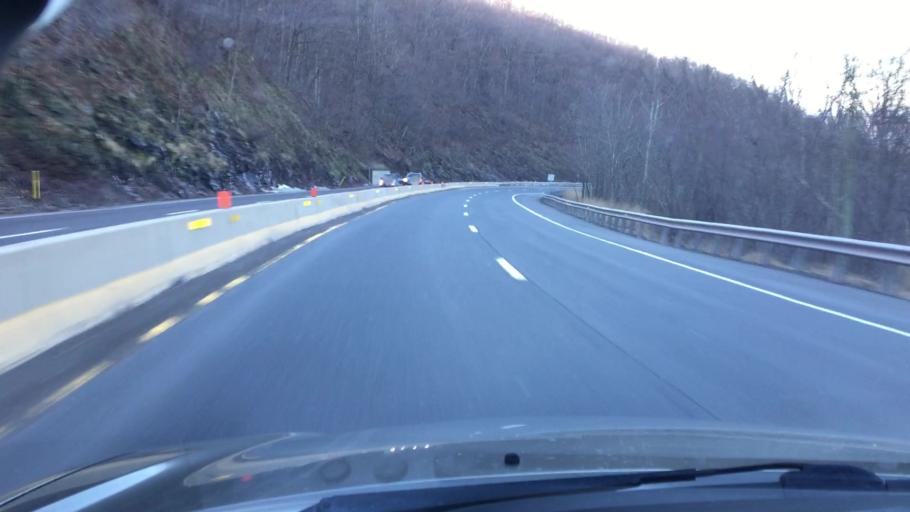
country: US
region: Pennsylvania
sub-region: Luzerne County
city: Mountain Top
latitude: 41.1811
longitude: -75.8886
